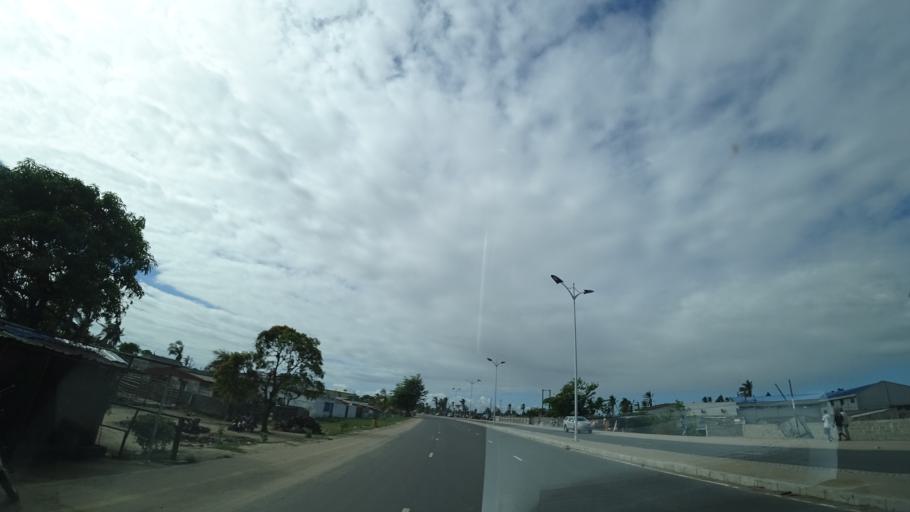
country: MZ
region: Sofala
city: Beira
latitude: -19.7784
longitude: 34.8815
